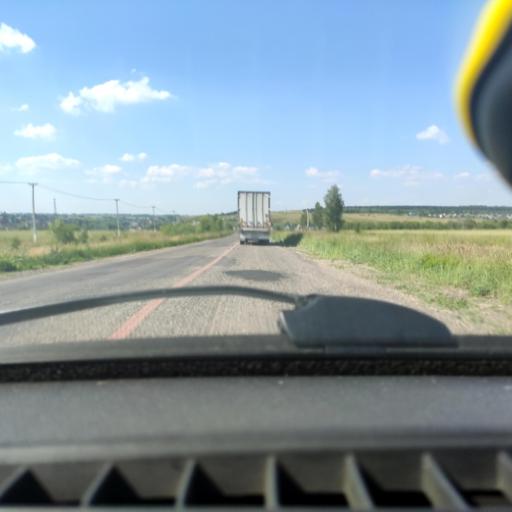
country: RU
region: Samara
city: Povolzhskiy
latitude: 53.7439
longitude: 49.7462
